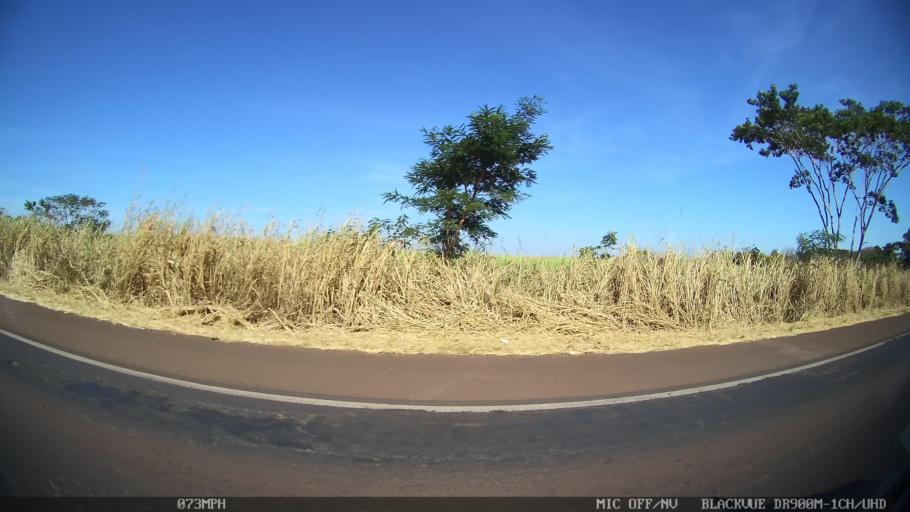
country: BR
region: Sao Paulo
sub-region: Barretos
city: Barretos
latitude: -20.4965
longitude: -48.5330
